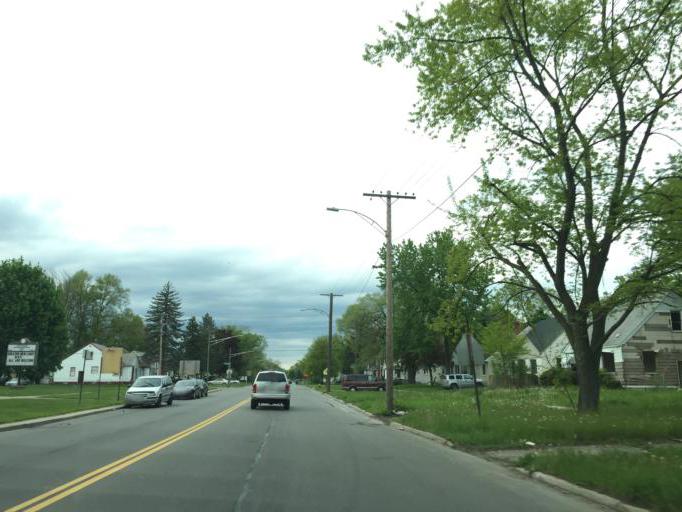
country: US
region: Michigan
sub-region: Wayne County
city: Redford
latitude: 42.3877
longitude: -83.2369
